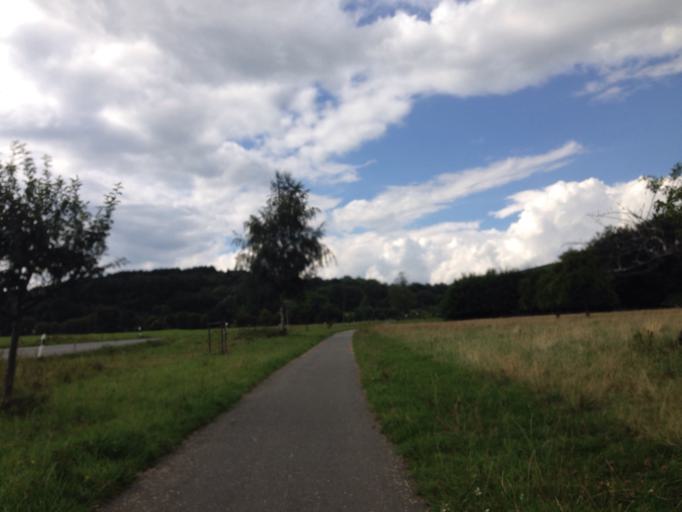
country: DE
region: Hesse
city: Mengerskirchen
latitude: 50.5510
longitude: 8.1706
